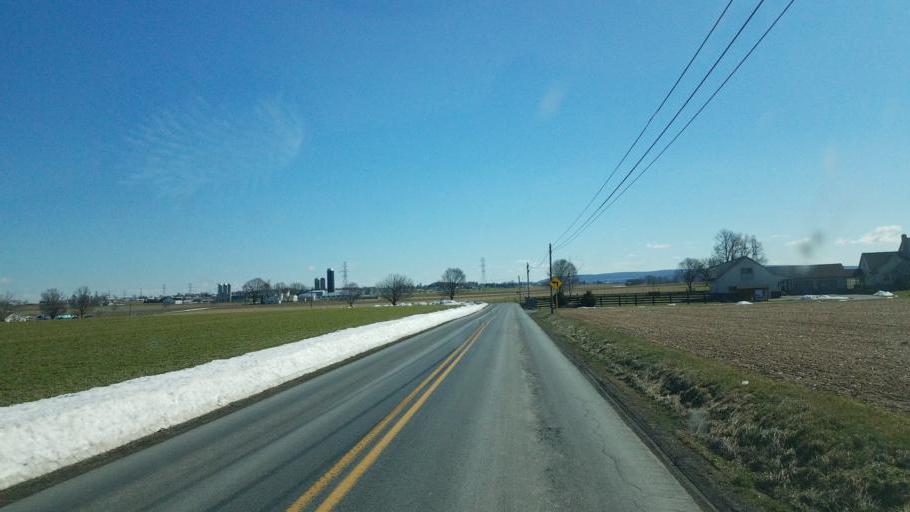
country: US
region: Pennsylvania
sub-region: Lancaster County
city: Intercourse
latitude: 40.0720
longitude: -76.1651
